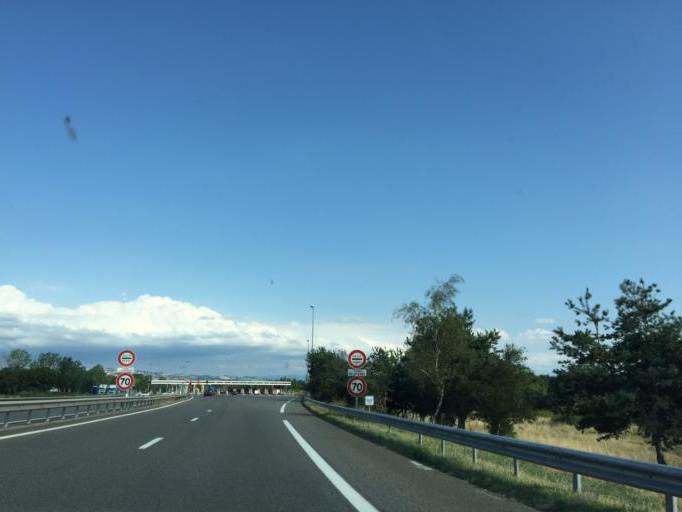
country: FR
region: Rhone-Alpes
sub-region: Departement de la Loire
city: Saint-Cyprien
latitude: 45.5623
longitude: 4.2376
